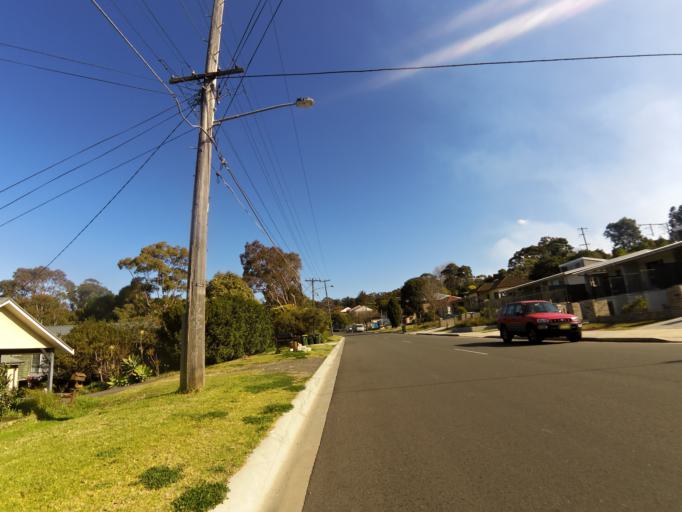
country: AU
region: New South Wales
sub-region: Sutherland Shire
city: Jannali
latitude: -34.0101
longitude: 151.0669
